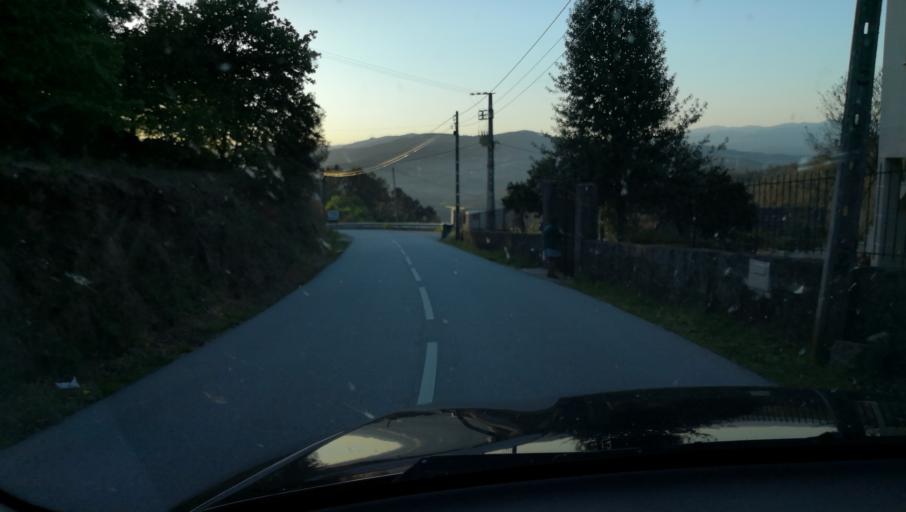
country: PT
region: Vila Real
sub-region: Mondim de Basto
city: Mondim de Basto
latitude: 41.4100
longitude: -7.9314
